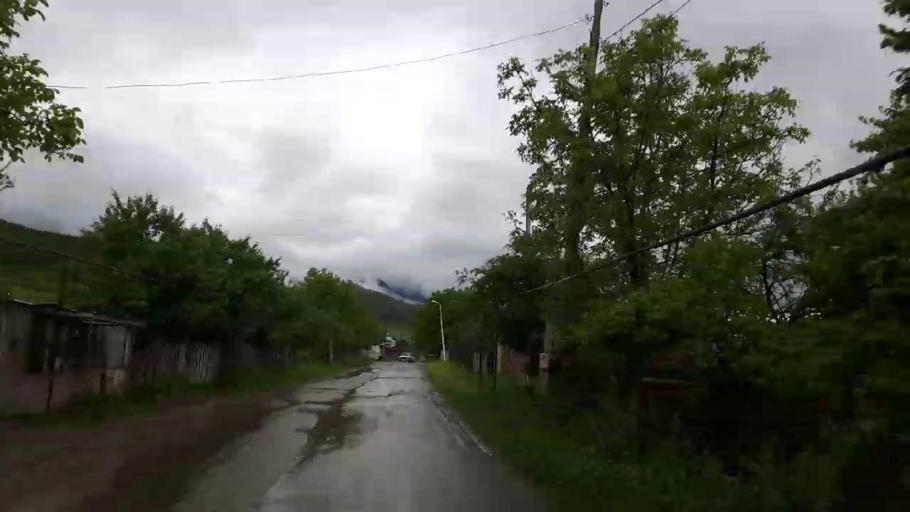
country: GE
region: Shida Kartli
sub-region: Khashuris Raioni
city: Khashuri
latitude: 41.9837
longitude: 43.6648
